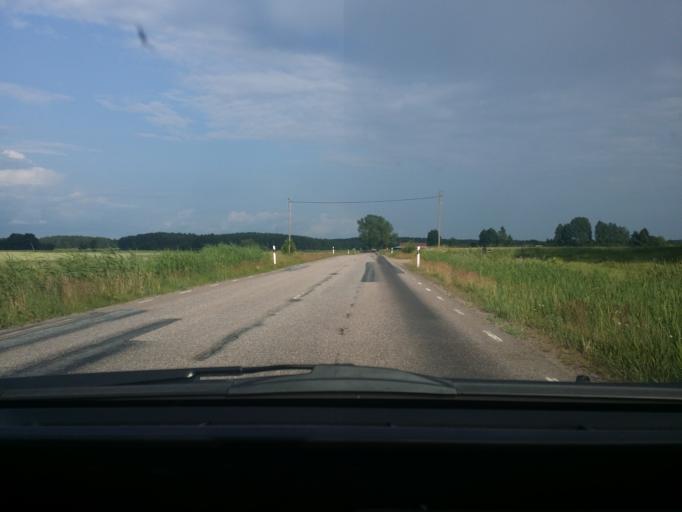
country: SE
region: Vaestmanland
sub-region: Hallstahammars Kommun
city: Kolback
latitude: 59.5583
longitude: 16.3317
